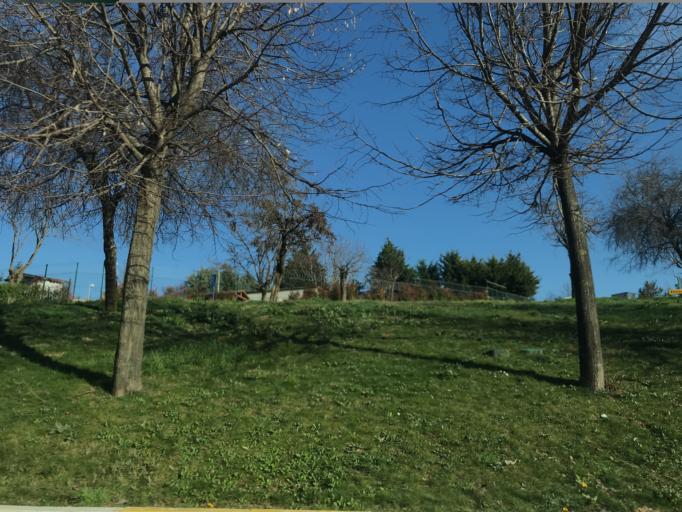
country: TR
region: Istanbul
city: Mahmutbey
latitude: 41.0323
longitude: 28.7779
